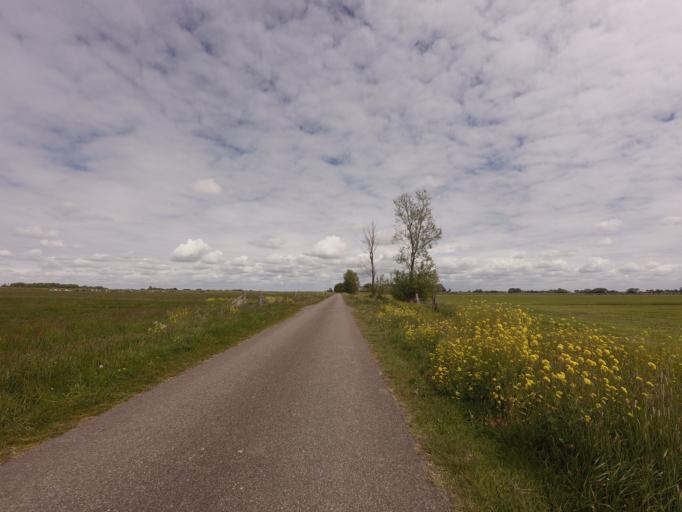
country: NL
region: Friesland
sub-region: Sudwest Fryslan
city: Koudum
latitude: 52.9126
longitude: 5.5089
